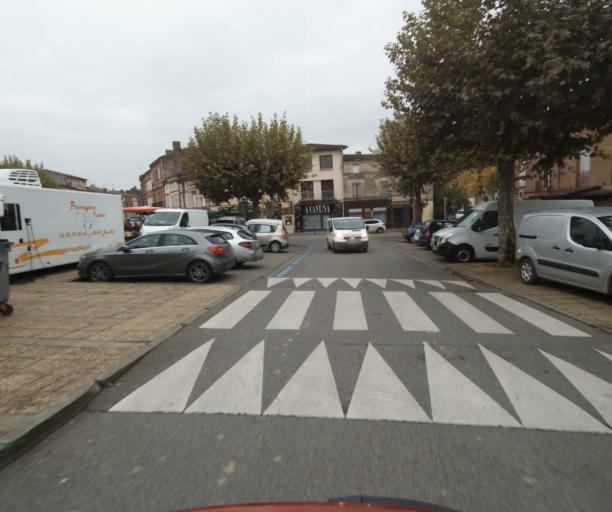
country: FR
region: Midi-Pyrenees
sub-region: Departement du Tarn-et-Garonne
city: Verdun-sur-Garonne
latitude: 43.8529
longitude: 1.2351
